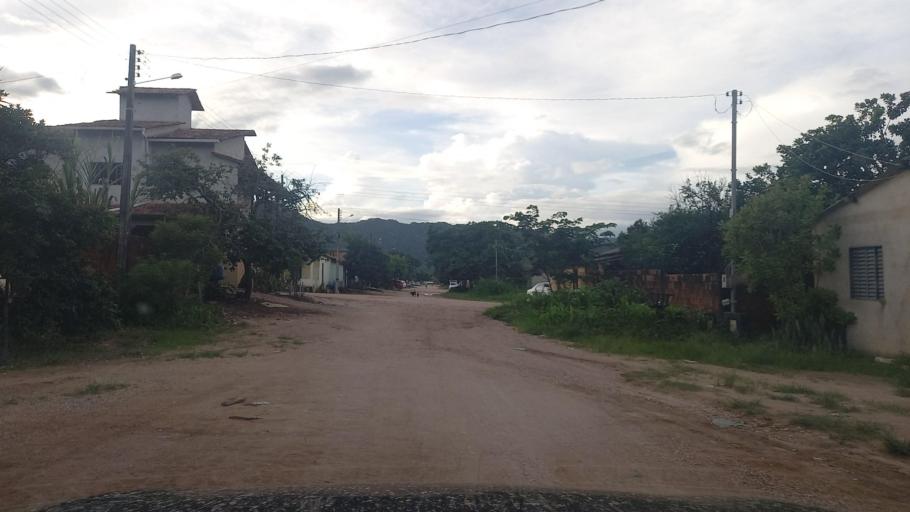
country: BR
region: Goias
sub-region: Cavalcante
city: Cavalcante
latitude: -13.7899
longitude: -47.4554
